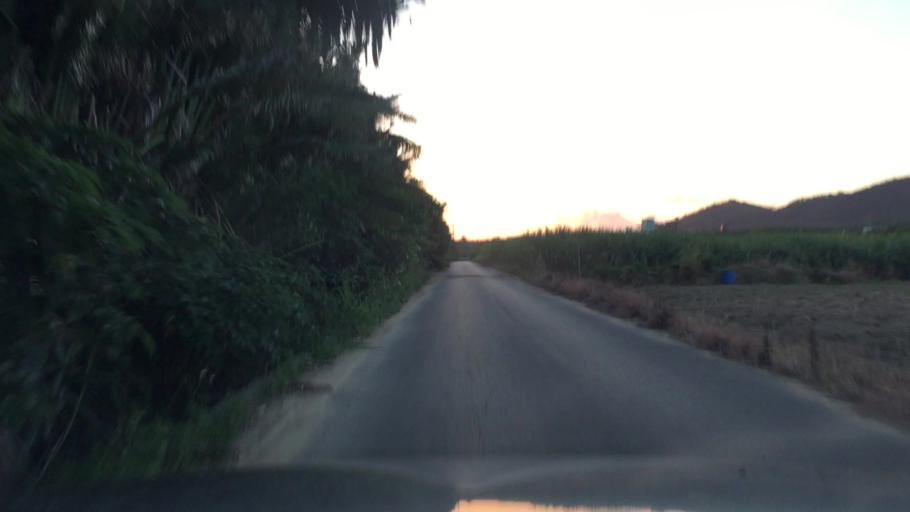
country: JP
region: Okinawa
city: Ishigaki
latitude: 24.3556
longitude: 124.1599
